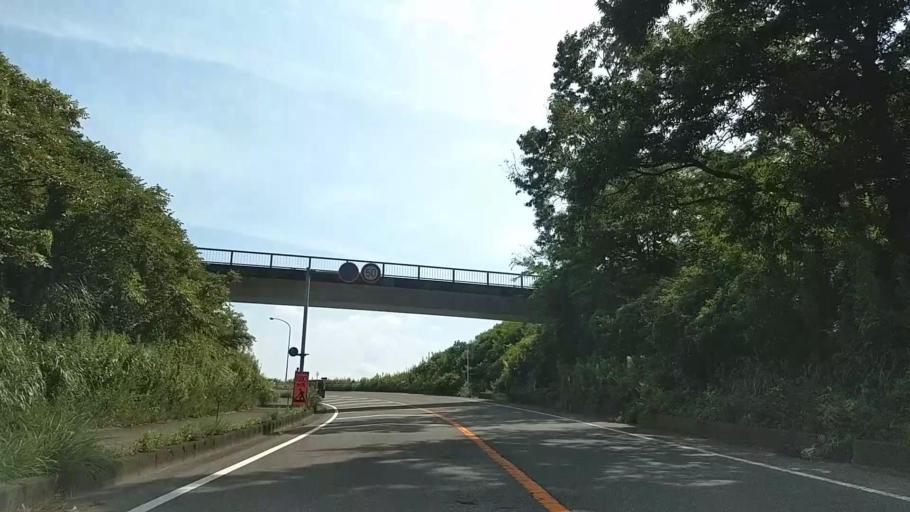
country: JP
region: Shizuoka
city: Mishima
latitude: 35.1355
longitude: 138.9585
